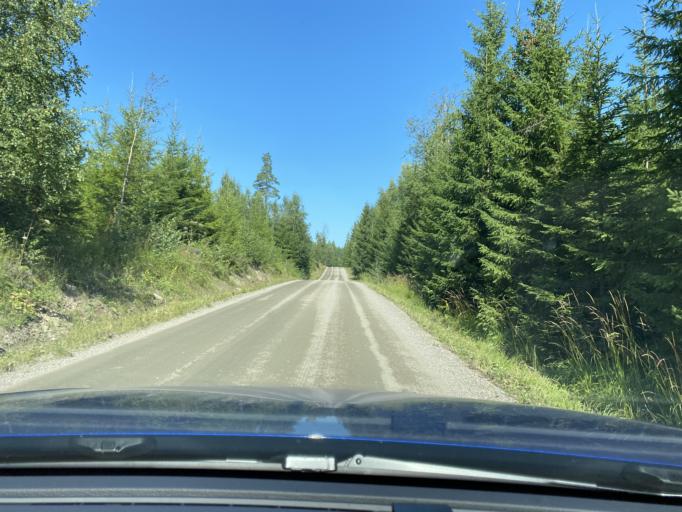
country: FI
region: Central Finland
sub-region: Jyvaeskylae
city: Korpilahti
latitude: 61.8672
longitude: 25.4236
